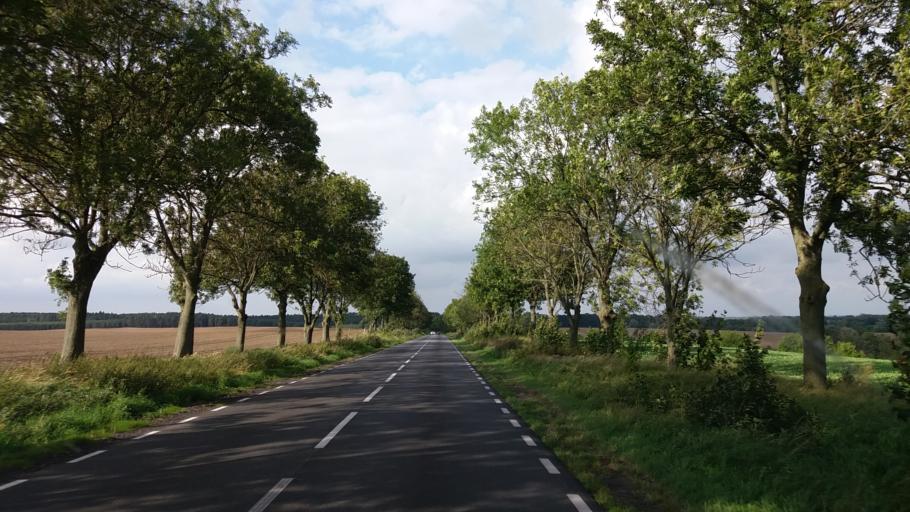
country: PL
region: West Pomeranian Voivodeship
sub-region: Powiat choszczenski
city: Pelczyce
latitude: 53.0535
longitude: 15.2999
